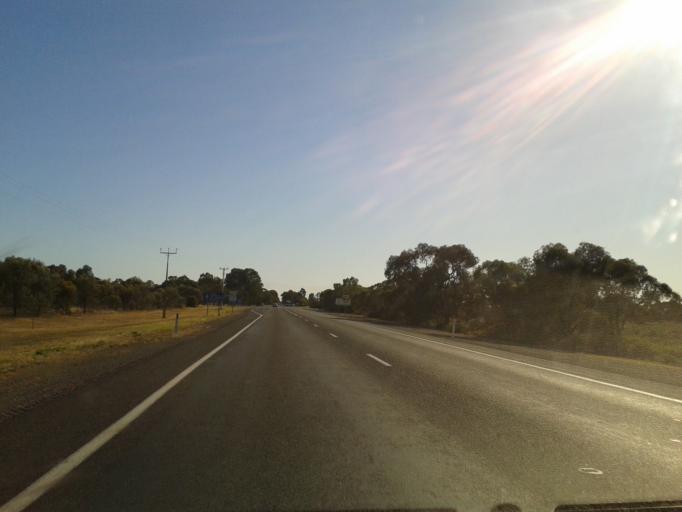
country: AU
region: South Australia
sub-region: Renmark Paringa
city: Renmark West
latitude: -34.2098
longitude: 140.6988
